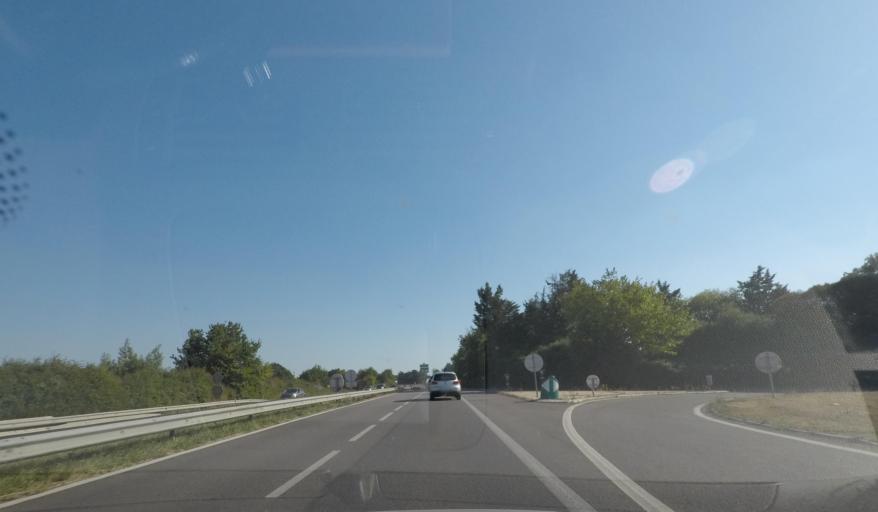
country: FR
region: Pays de la Loire
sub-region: Departement de la Loire-Atlantique
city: Saint-Michel-Chef-Chef
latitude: 47.1885
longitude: -2.1469
